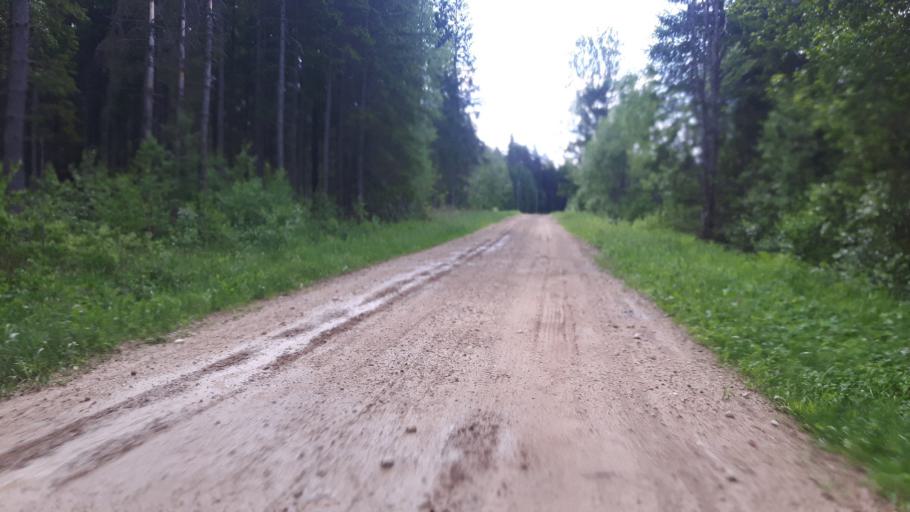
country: EE
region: Paernumaa
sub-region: Vaendra vald (alev)
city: Vandra
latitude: 58.7248
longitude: 25.0353
